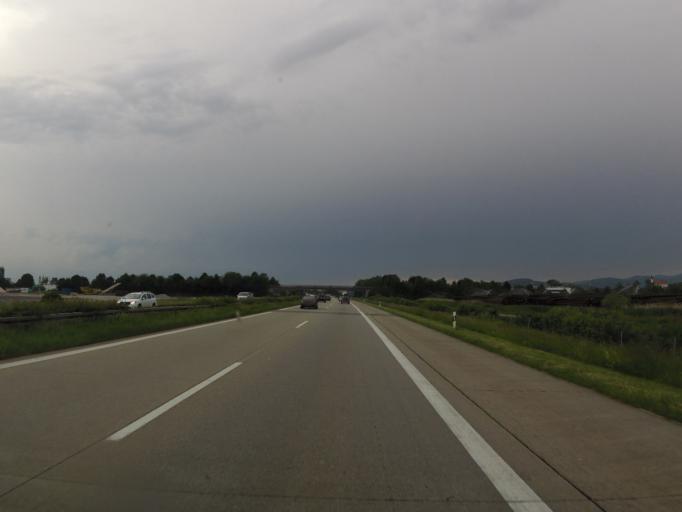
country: DE
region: Bavaria
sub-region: Lower Bavaria
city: Hengersberg
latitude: 48.7619
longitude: 13.0594
